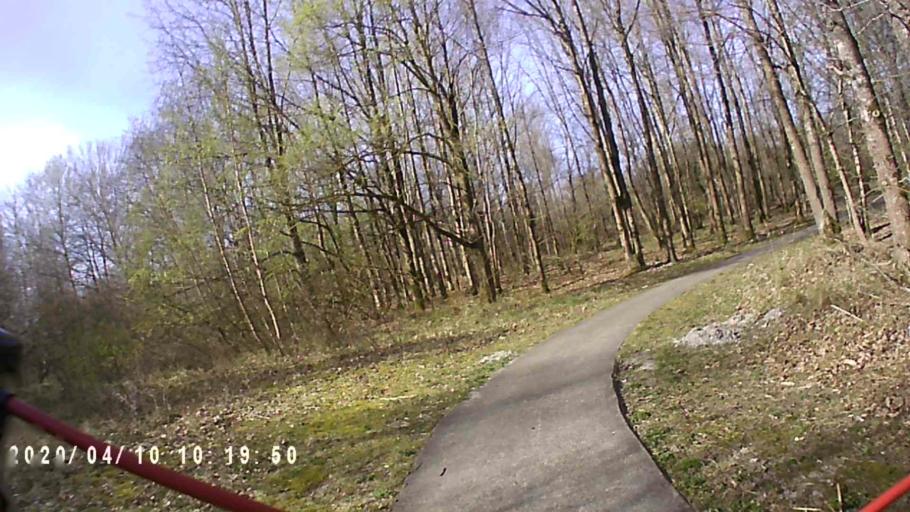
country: NL
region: Friesland
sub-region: Gemeente Dongeradeel
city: Anjum
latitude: 53.3800
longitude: 6.2224
